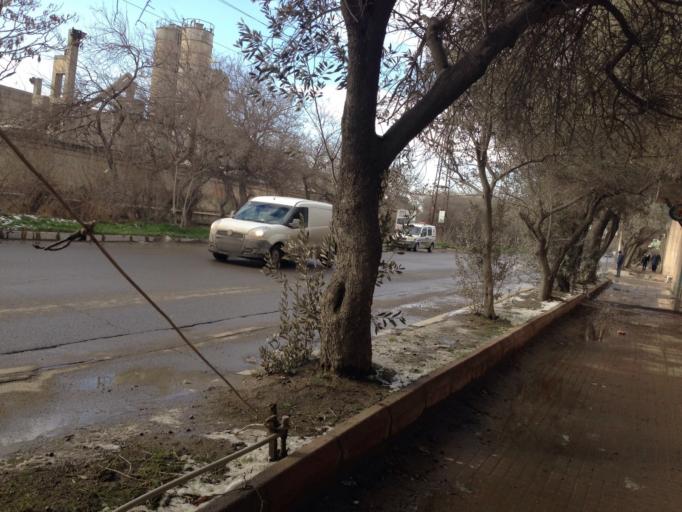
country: AZ
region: Baki
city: Baku
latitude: 40.3991
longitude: 49.8900
